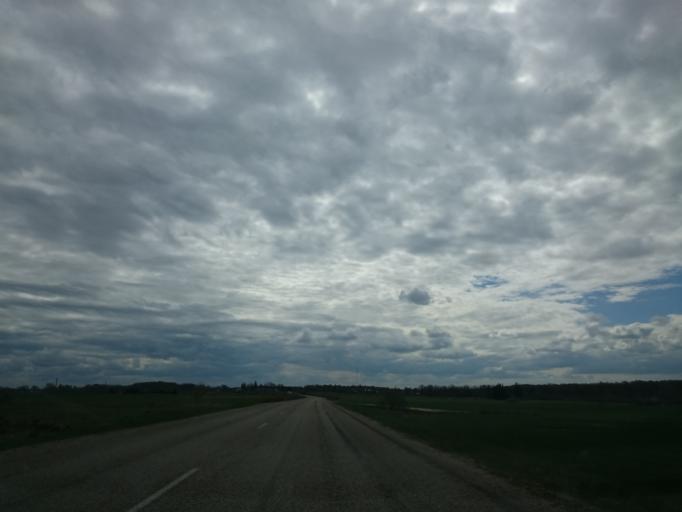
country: LV
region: Aizpute
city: Aizpute
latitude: 56.7531
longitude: 21.6143
